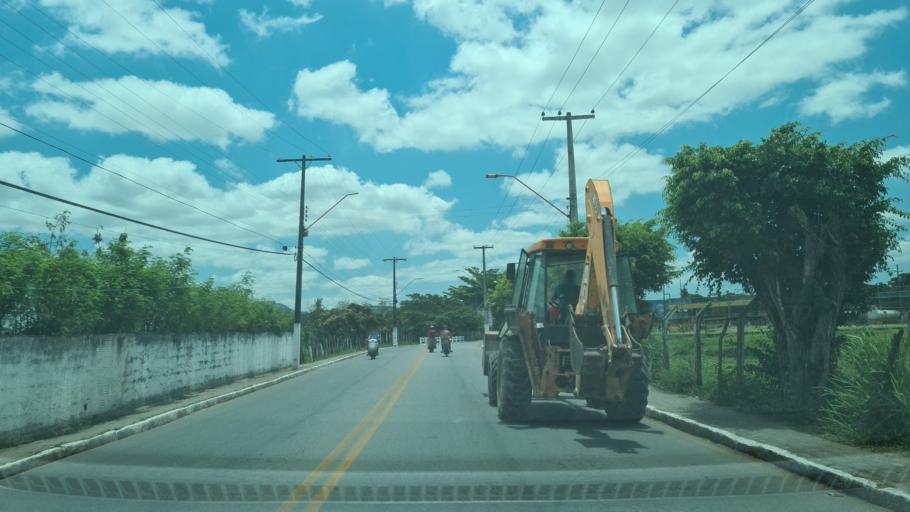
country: BR
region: Alagoas
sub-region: Uniao Dos Palmares
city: Uniao dos Palmares
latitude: -9.1648
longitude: -36.0261
